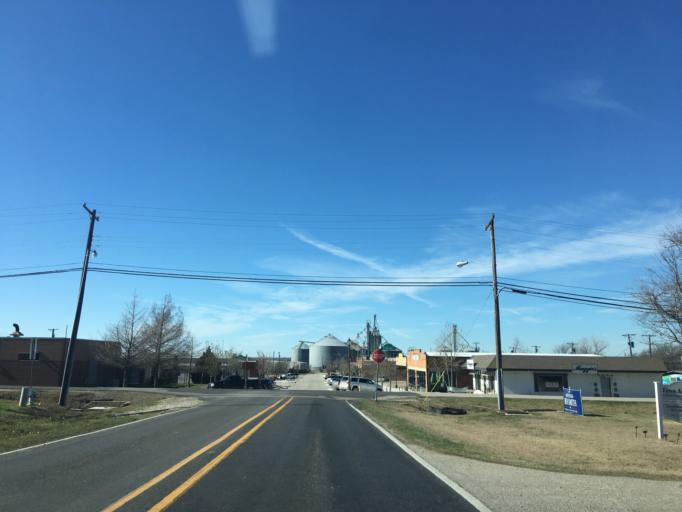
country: US
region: Texas
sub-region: Collin County
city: Prosper
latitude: 33.2361
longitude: -96.8014
